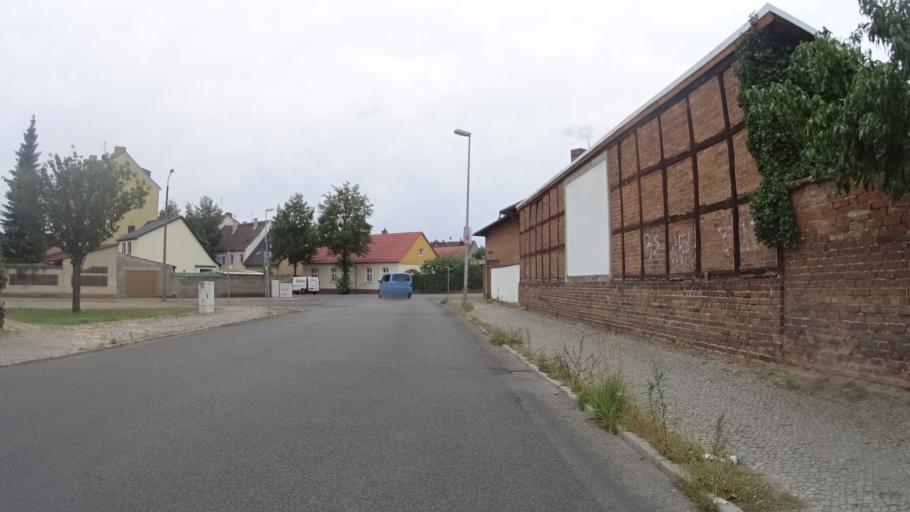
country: DE
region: Brandenburg
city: Luckenwalde
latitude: 52.0864
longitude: 13.1597
